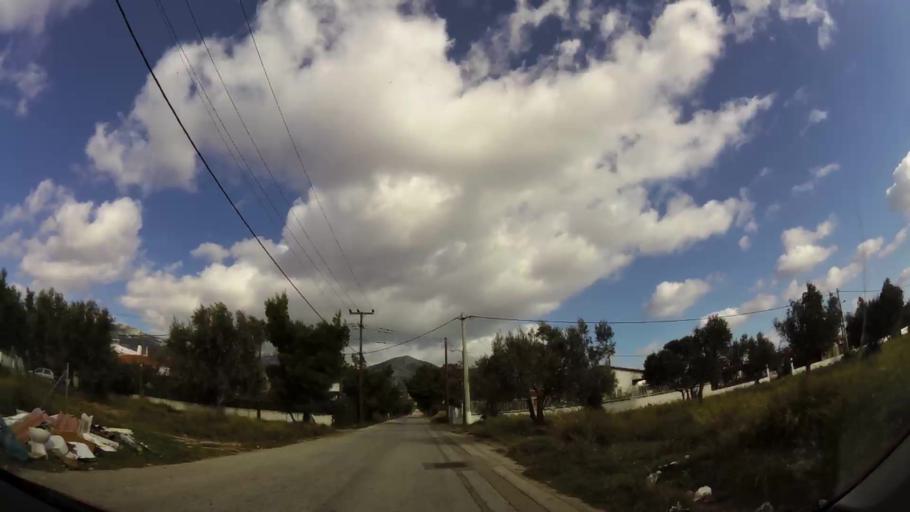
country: GR
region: Attica
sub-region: Nomarchia Anatolikis Attikis
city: Thrakomakedones
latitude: 38.1157
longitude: 23.7565
